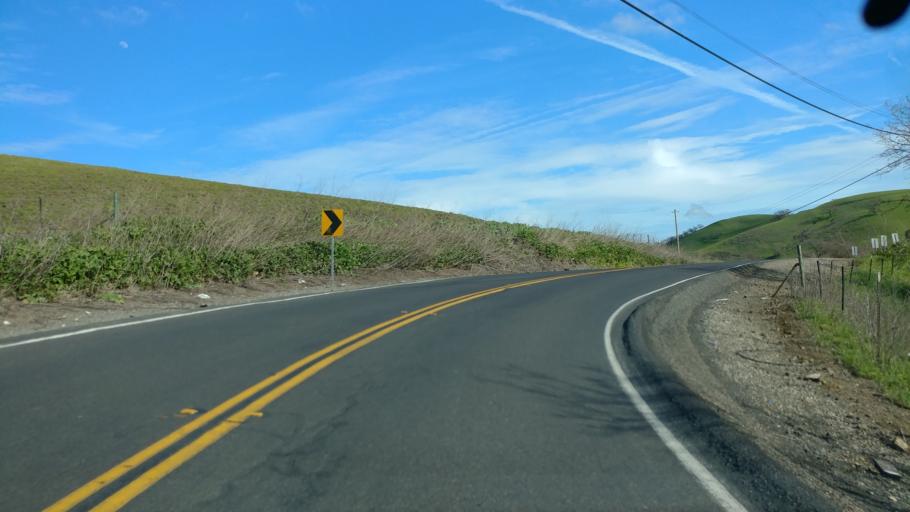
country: US
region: California
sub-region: Contra Costa County
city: Blackhawk
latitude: 37.7799
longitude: -121.8357
